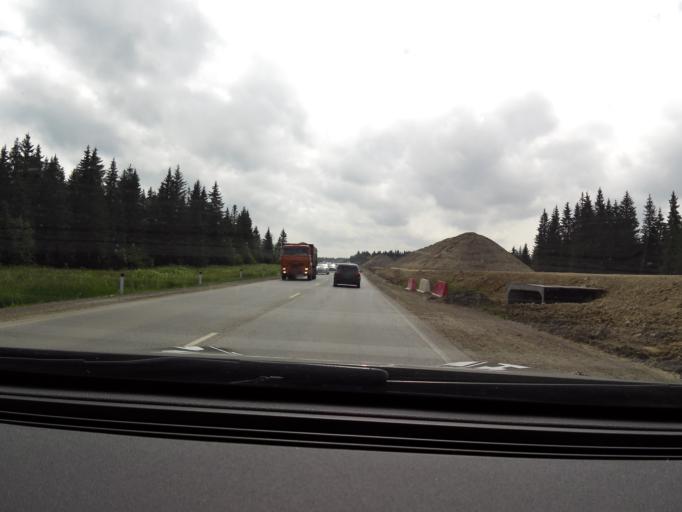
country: RU
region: Perm
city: Kukushtan
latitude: 57.6474
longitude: 56.4455
